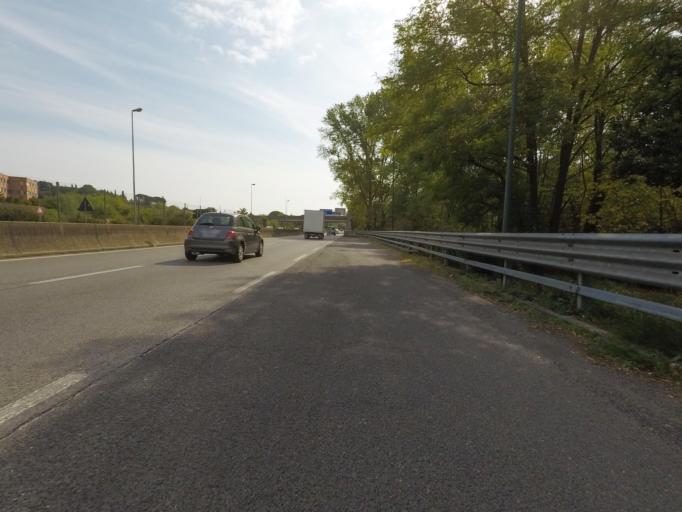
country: IT
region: Tuscany
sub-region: Provincia di Siena
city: Siena
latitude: 43.3097
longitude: 11.3129
